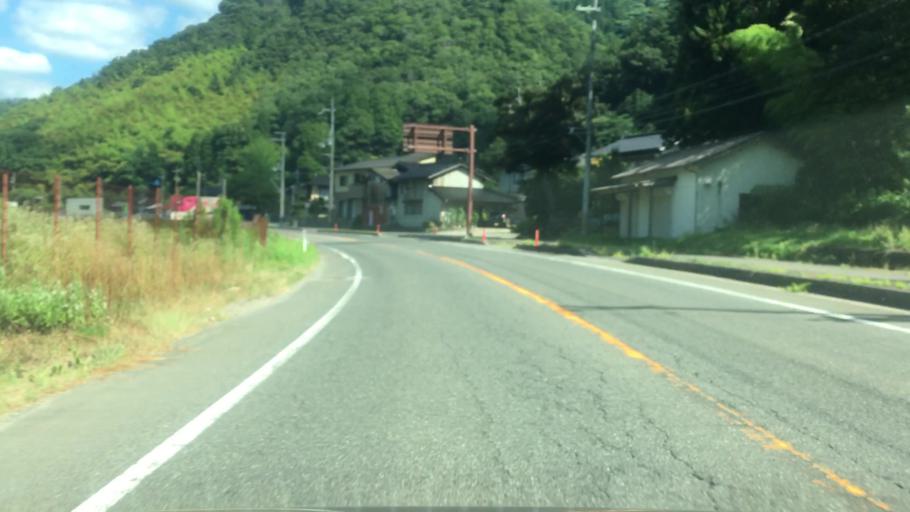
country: JP
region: Hyogo
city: Toyooka
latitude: 35.5697
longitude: 134.7812
